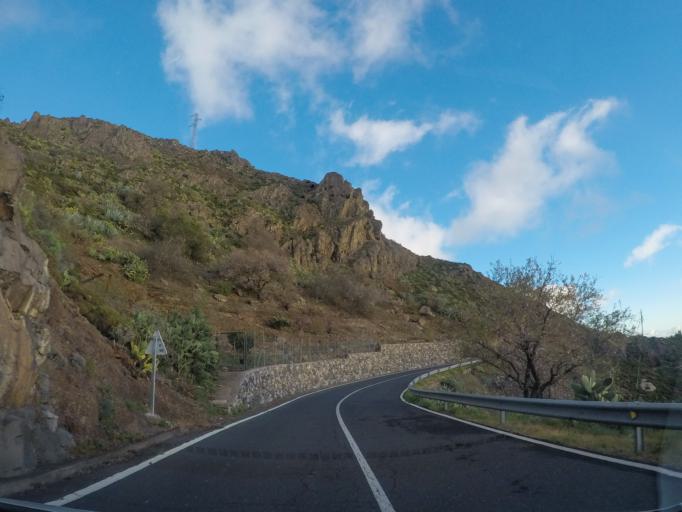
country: ES
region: Canary Islands
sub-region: Provincia de Santa Cruz de Tenerife
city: Alajero
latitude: 28.0793
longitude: -17.2433
